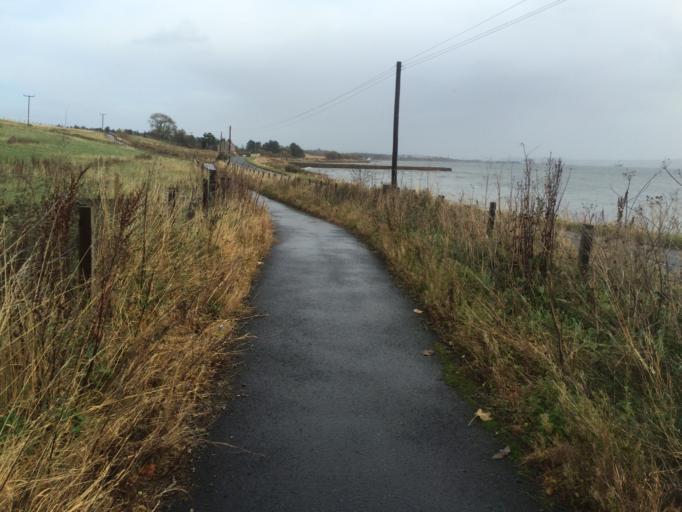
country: GB
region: Scotland
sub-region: Highland
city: Alness
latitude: 57.6899
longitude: -4.2327
